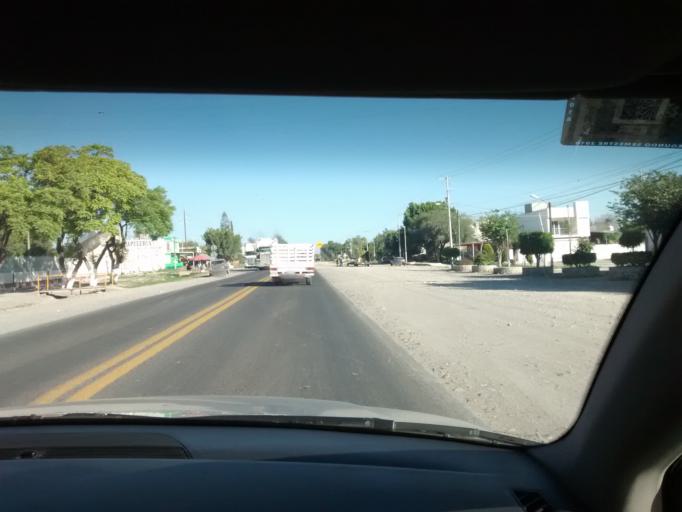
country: MX
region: Puebla
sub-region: Tehuacan
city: Magdalena Cuayucatepec
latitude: 18.5125
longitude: -97.4945
